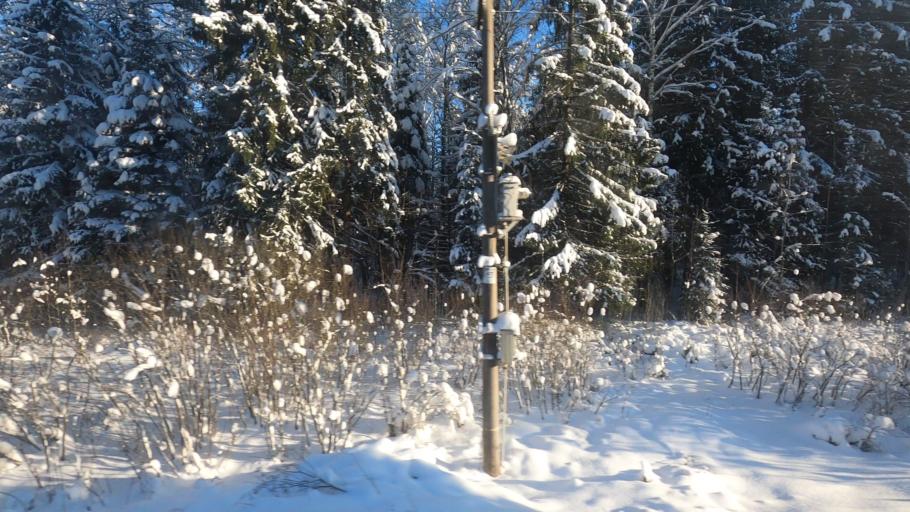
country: RU
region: Moskovskaya
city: Novo-Nikol'skoye
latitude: 56.5677
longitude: 37.5669
